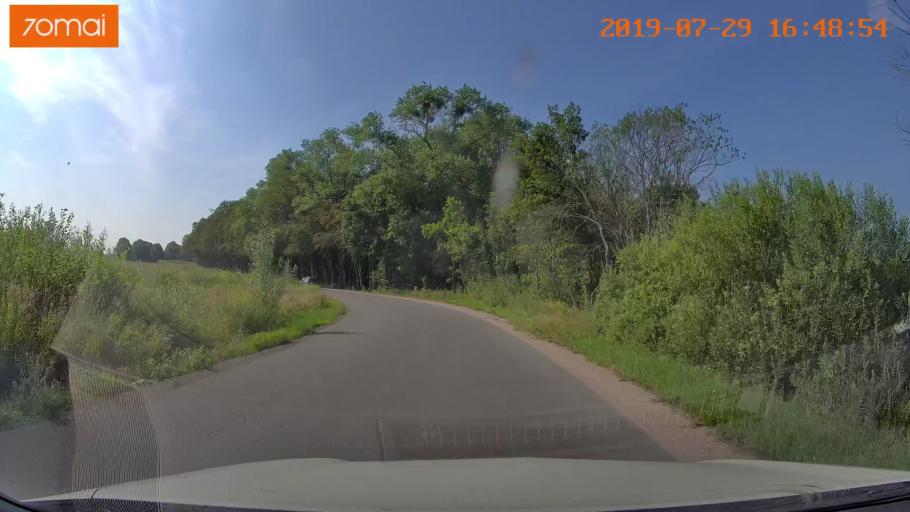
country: RU
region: Kaliningrad
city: Primorsk
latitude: 54.7905
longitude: 20.0716
